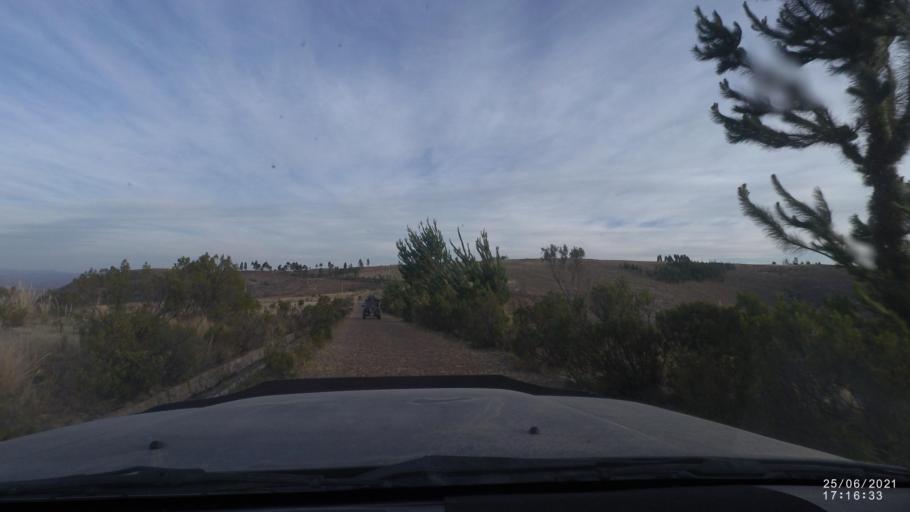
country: BO
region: Cochabamba
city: Arani
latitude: -17.8812
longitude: -65.7006
